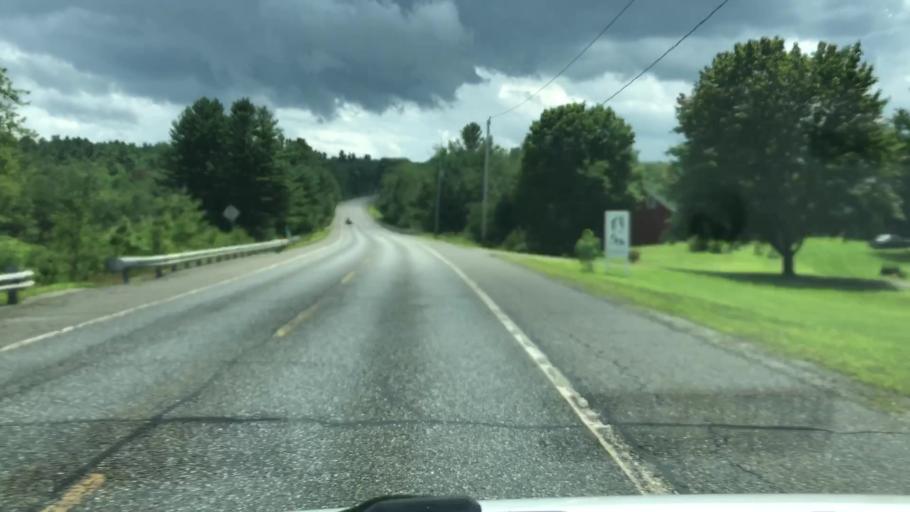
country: US
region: Massachusetts
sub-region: Franklin County
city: Ashfield
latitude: 42.4688
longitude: -72.8091
